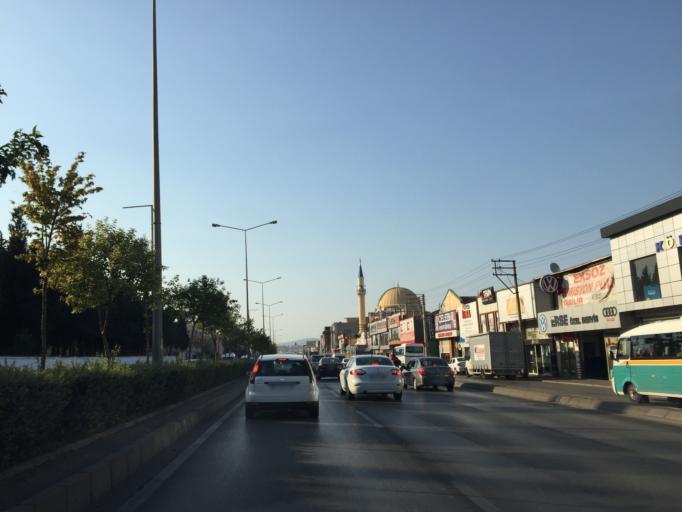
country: TR
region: Izmir
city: Karabaglar
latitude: 38.3665
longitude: 27.1369
